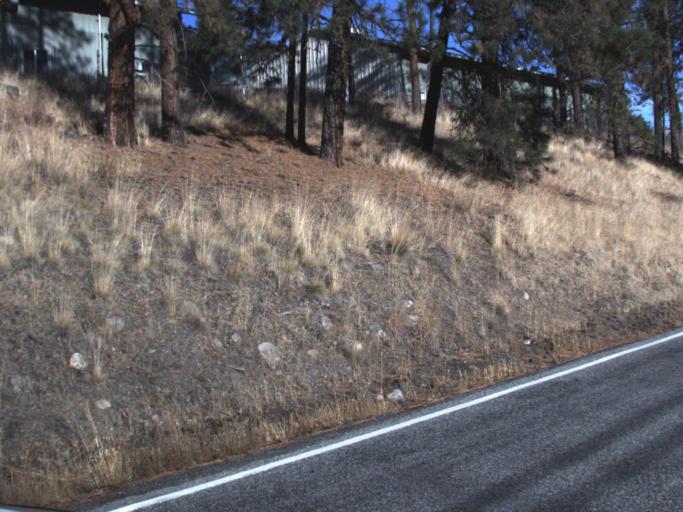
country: US
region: Washington
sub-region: Ferry County
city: Republic
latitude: 48.6268
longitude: -118.7319
